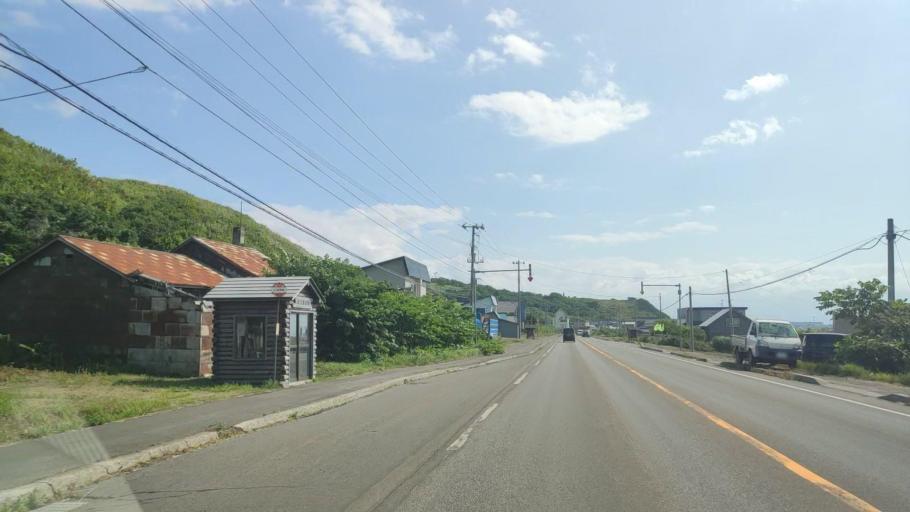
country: JP
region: Hokkaido
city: Rumoi
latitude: 43.9692
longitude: 141.6466
